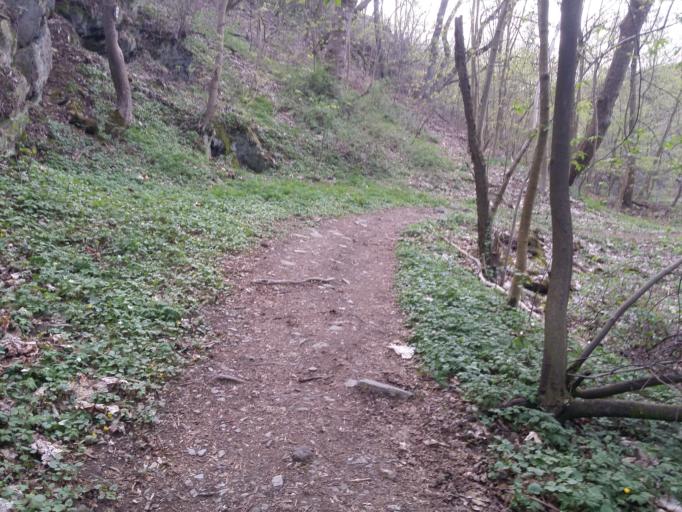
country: DE
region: Saxony-Anhalt
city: Harzgerode
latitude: 51.6679
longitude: 11.1338
